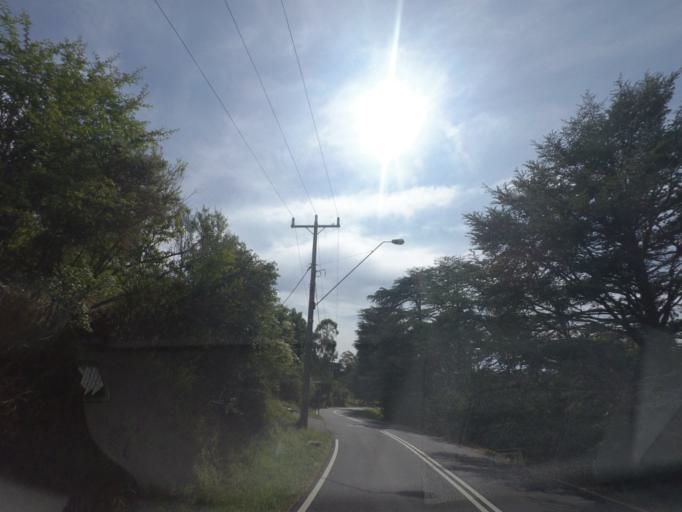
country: AU
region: Victoria
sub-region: Banyule
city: Viewbank
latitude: -37.7384
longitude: 145.1024
